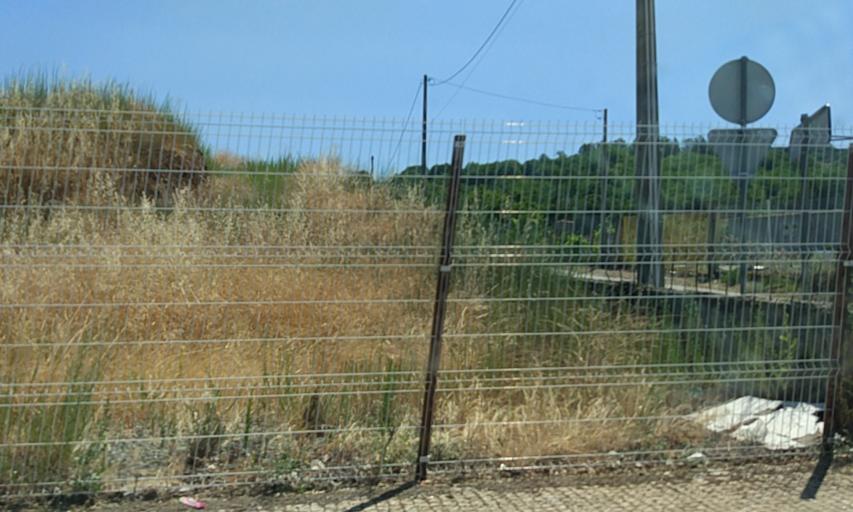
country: PT
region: Braganca
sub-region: Braganca Municipality
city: Braganca
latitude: 41.7804
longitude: -6.7805
